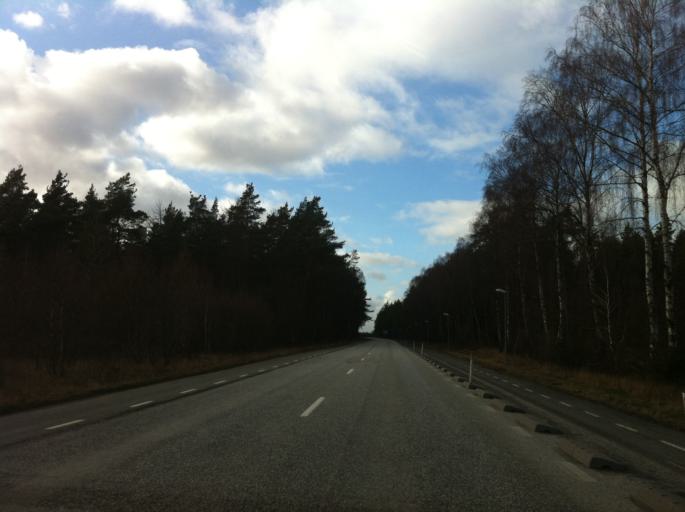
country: SE
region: Blekinge
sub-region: Solvesborgs Kommun
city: Soelvesborg
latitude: 56.0538
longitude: 14.5681
